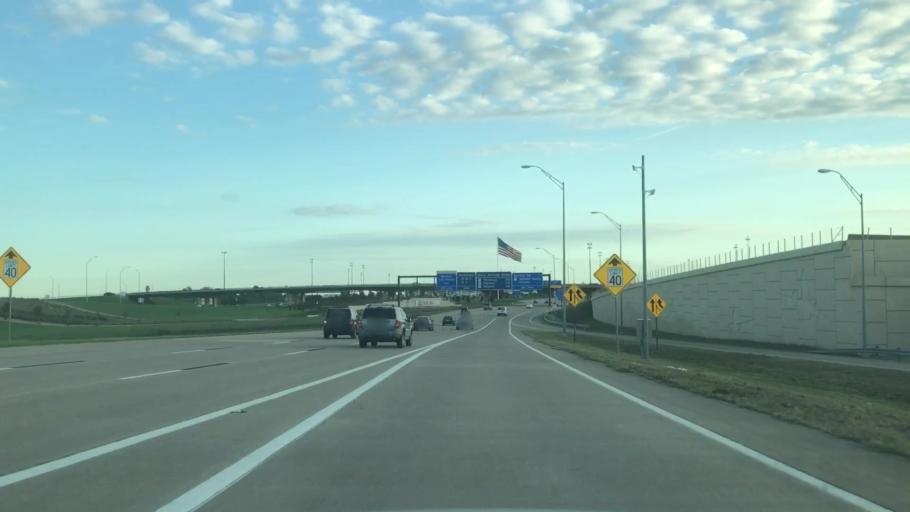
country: US
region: Texas
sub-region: Dallas County
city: Coppell
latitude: 32.9293
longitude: -97.0413
